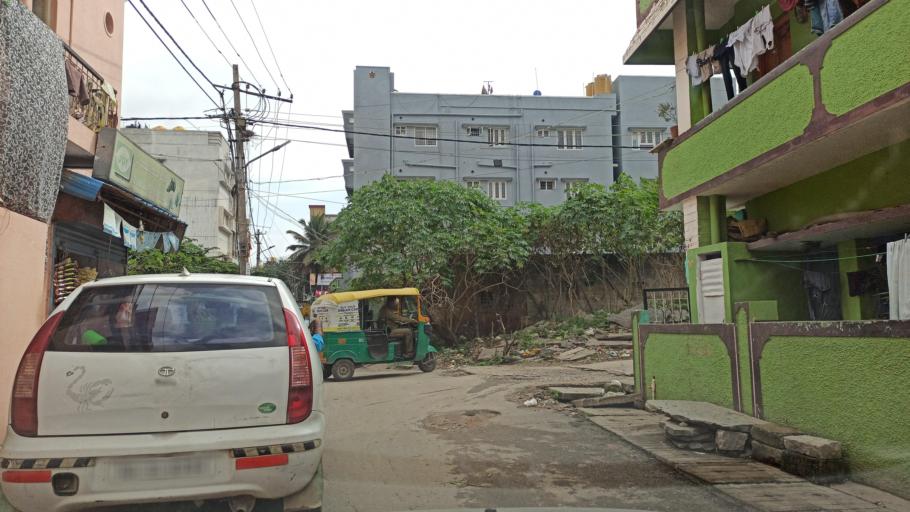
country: IN
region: Karnataka
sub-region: Bangalore Urban
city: Bangalore
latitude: 13.0034
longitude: 77.6724
